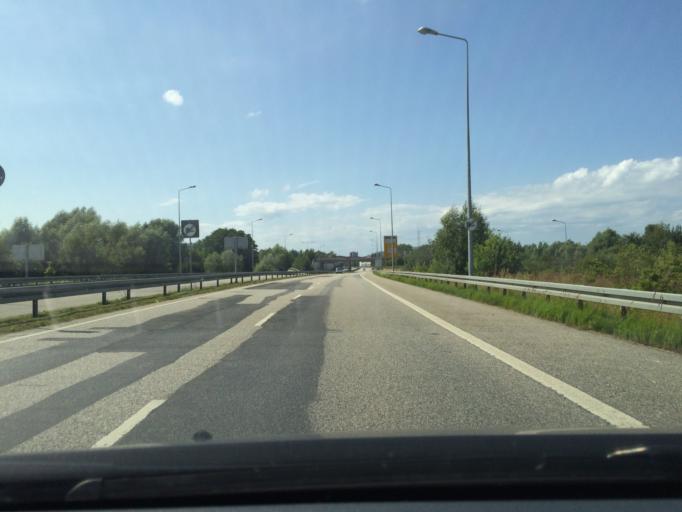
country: DE
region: Mecklenburg-Vorpommern
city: Warnemuende
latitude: 54.1355
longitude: 12.0834
